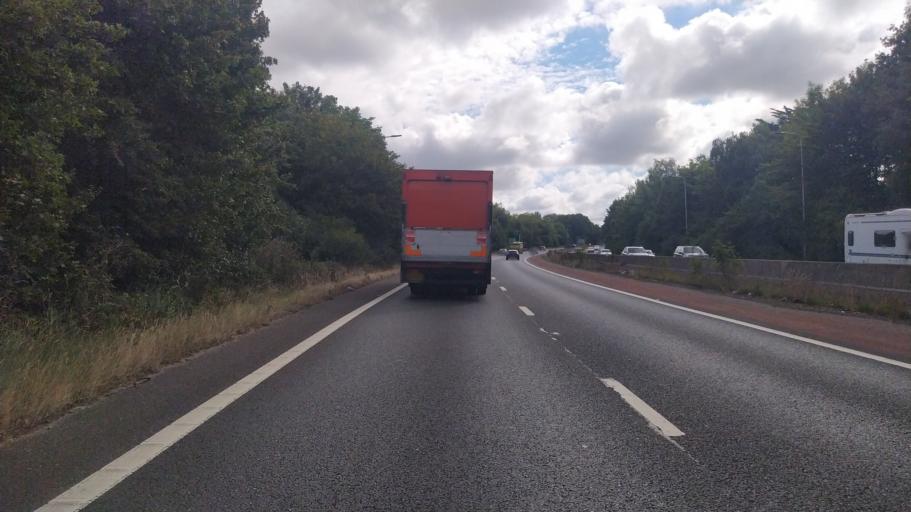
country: GB
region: England
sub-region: Hampshire
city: Havant
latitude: 50.8484
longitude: -1.0007
